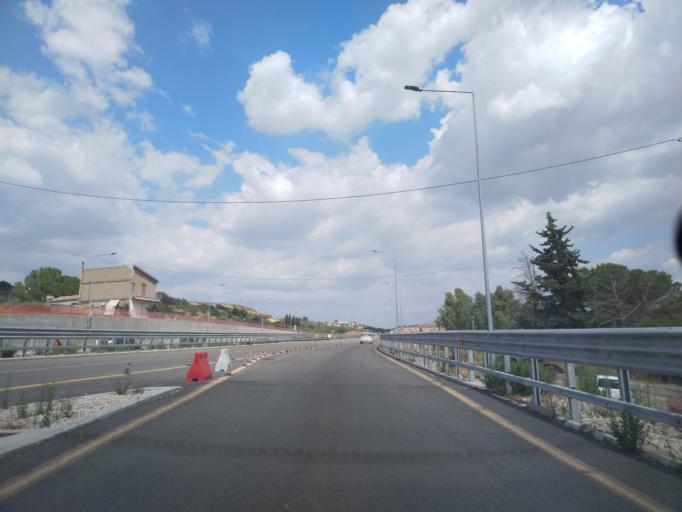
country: IT
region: Sicily
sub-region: Provincia di Caltanissetta
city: San Cataldo
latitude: 37.4505
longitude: 13.9716
